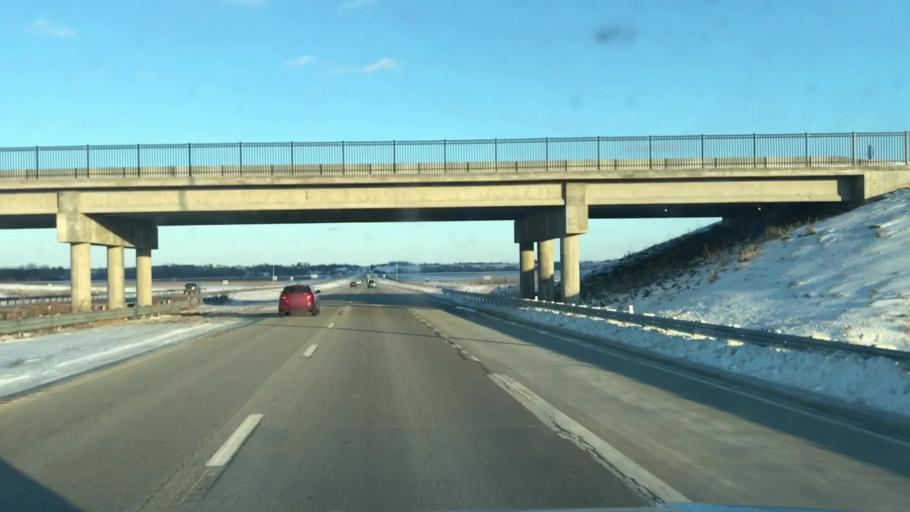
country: US
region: Missouri
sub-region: Buchanan County
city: Saint Joseph
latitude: 39.7479
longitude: -94.7504
